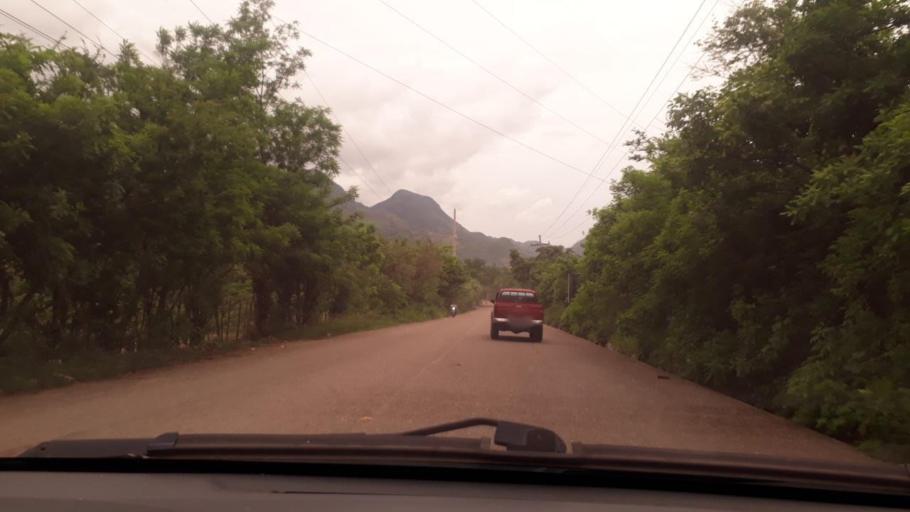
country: GT
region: Chiquimula
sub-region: Municipio de Jocotan
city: Jocotan
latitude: 14.7980
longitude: -89.3949
